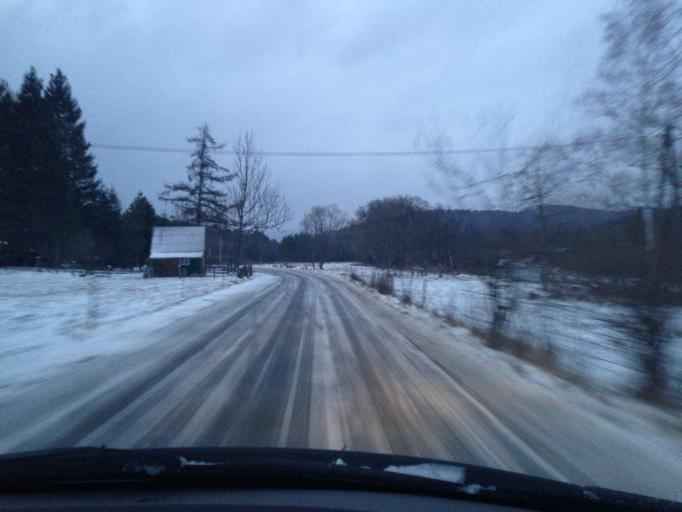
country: PL
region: Subcarpathian Voivodeship
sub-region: Powiat jasielski
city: Krempna
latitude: 49.5068
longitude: 21.5137
